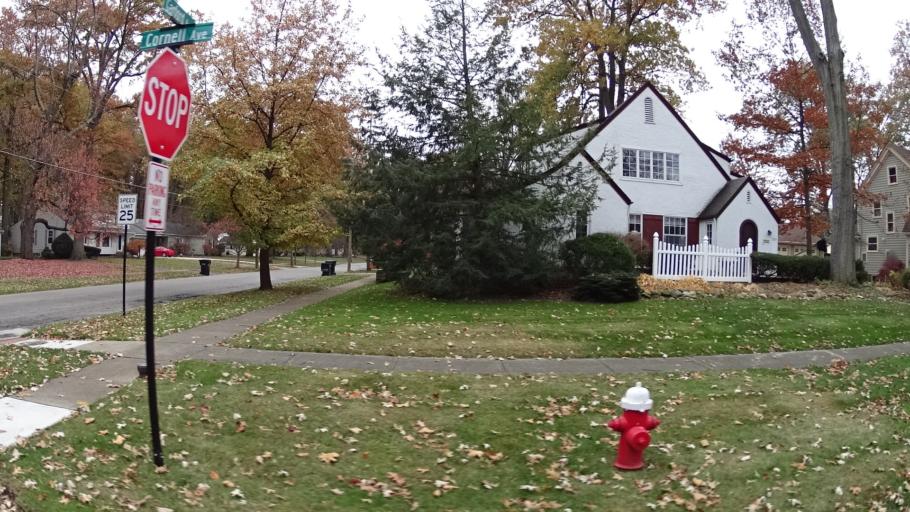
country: US
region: Ohio
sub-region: Lorain County
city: Elyria
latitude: 41.3612
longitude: -82.0918
